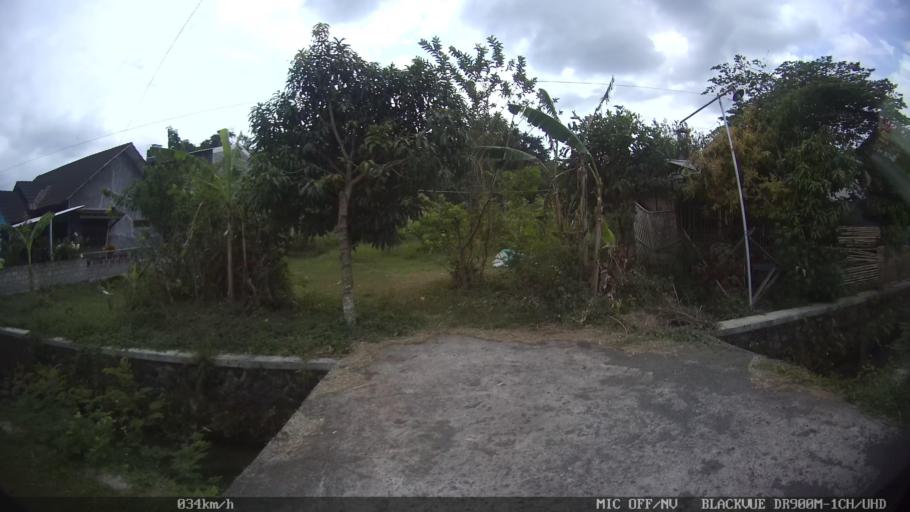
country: ID
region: Daerah Istimewa Yogyakarta
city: Depok
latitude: -7.8131
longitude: 110.4691
